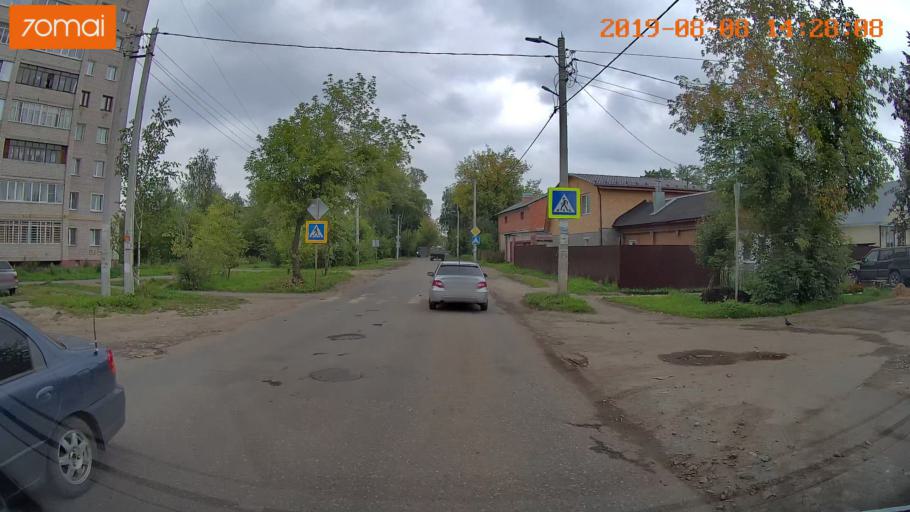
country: RU
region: Ivanovo
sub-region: Gorod Ivanovo
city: Ivanovo
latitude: 56.9969
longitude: 40.9461
